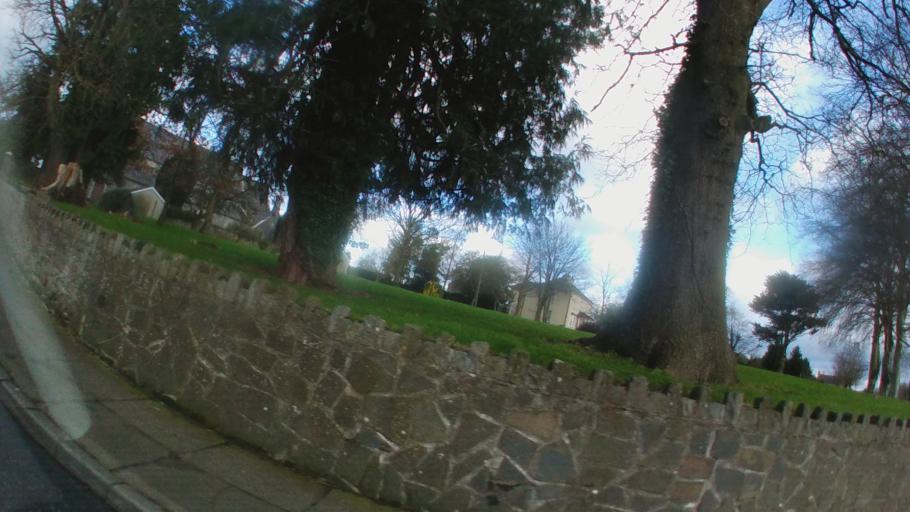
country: IE
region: Leinster
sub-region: Kilkenny
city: Thomastown
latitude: 52.6281
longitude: -7.0763
